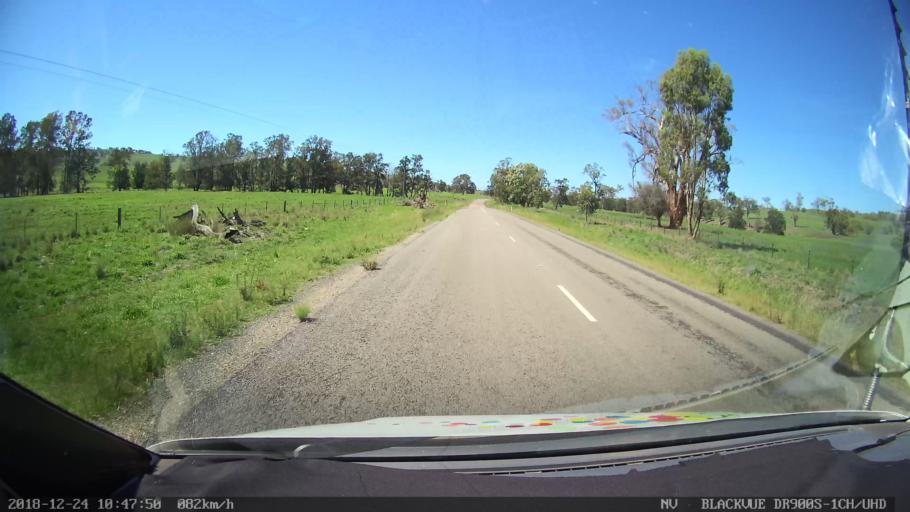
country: AU
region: New South Wales
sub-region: Upper Hunter Shire
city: Merriwa
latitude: -31.9292
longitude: 150.4298
